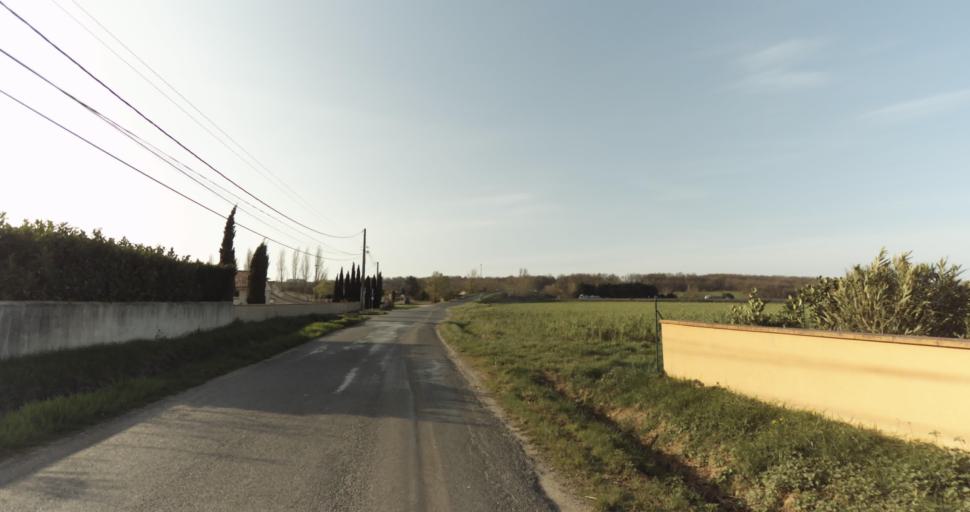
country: FR
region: Midi-Pyrenees
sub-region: Departement du Tarn
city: Saint-Sulpice-la-Pointe
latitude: 43.7566
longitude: 1.6875
